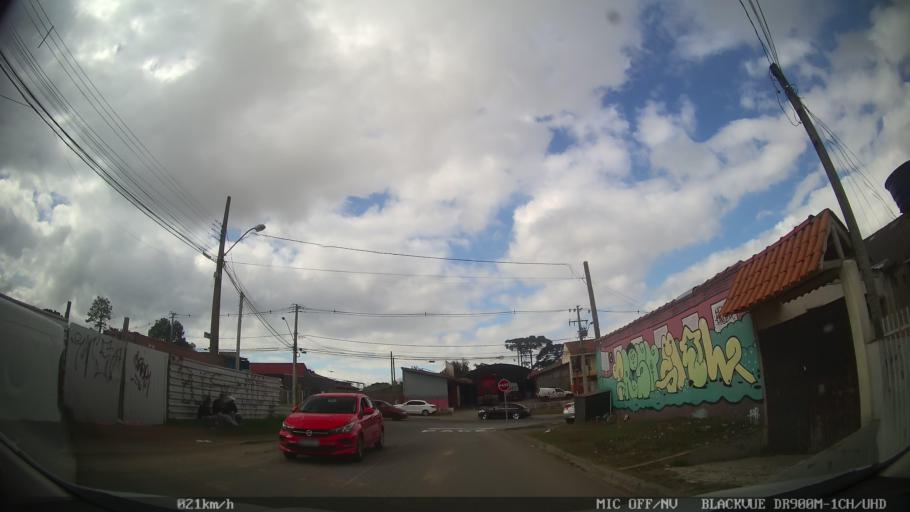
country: BR
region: Parana
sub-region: Colombo
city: Colombo
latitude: -25.3570
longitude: -49.2011
